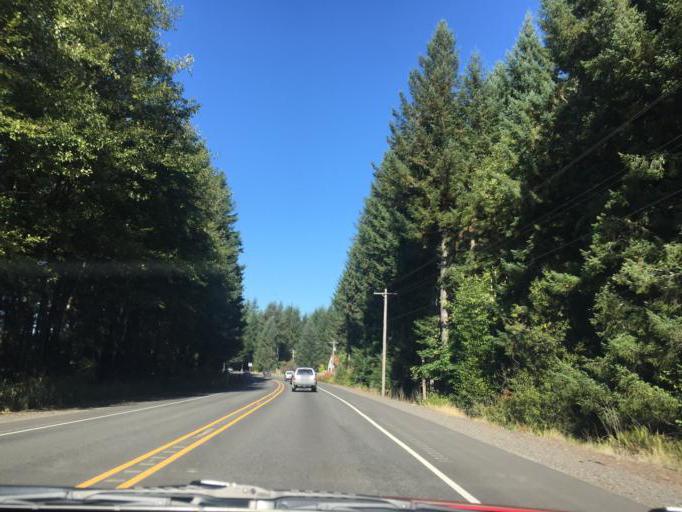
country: US
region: Oregon
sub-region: Columbia County
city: Vernonia
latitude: 45.7342
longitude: -123.2567
